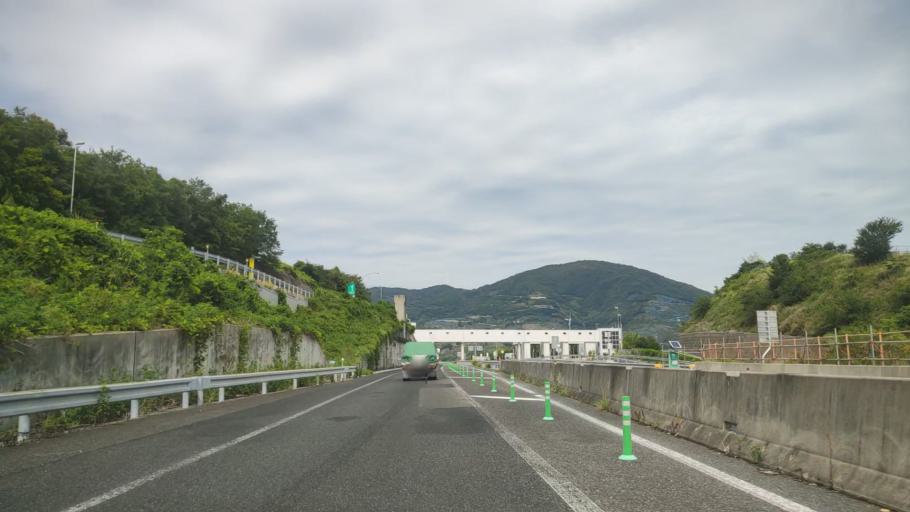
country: JP
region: Wakayama
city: Kainan
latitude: 34.0594
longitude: 135.2005
